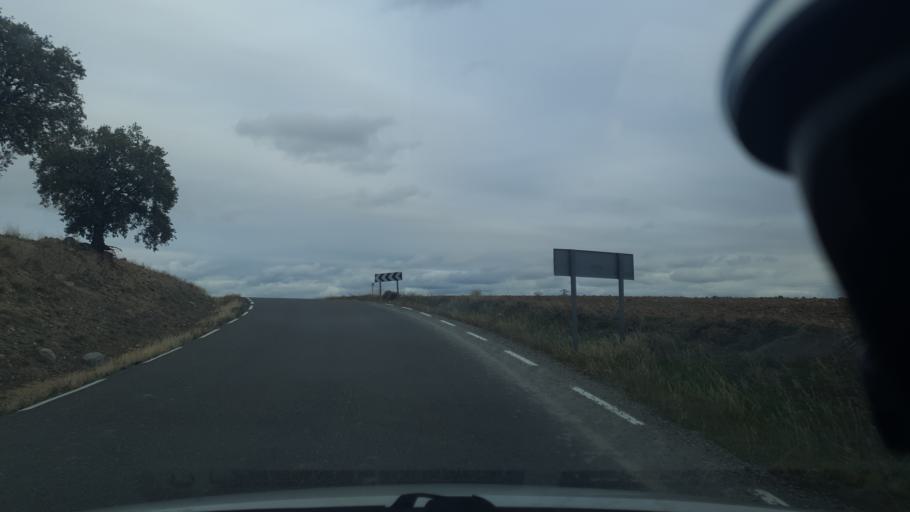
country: ES
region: Castille and Leon
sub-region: Provincia de Avila
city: Gotarrendura
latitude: 40.8264
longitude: -4.7130
